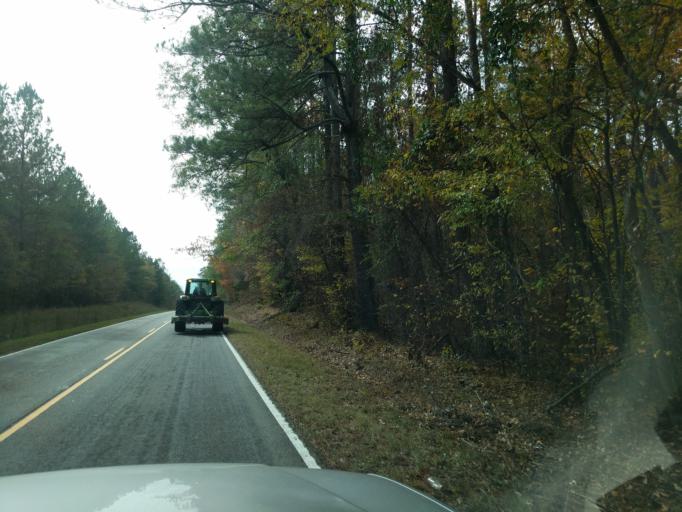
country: US
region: South Carolina
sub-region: Laurens County
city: Joanna
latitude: 34.2811
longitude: -81.8484
